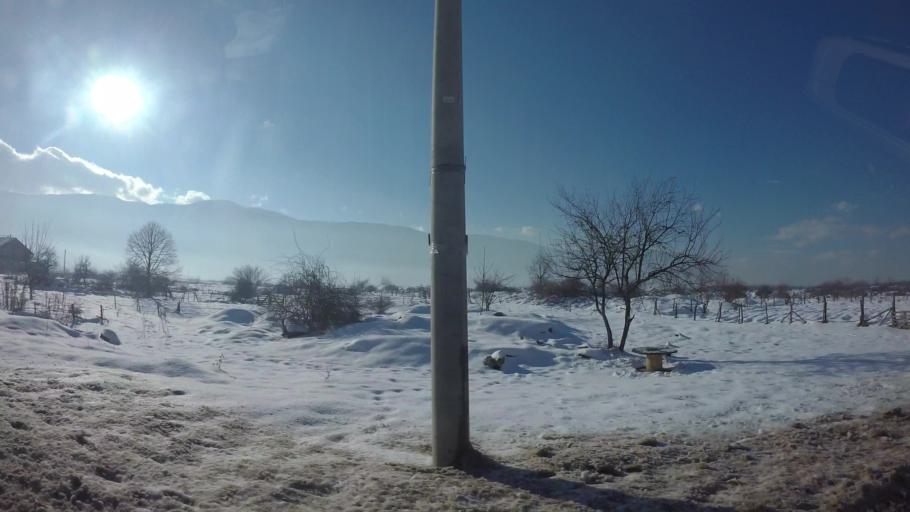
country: BA
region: Federation of Bosnia and Herzegovina
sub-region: Kanton Sarajevo
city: Sarajevo
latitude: 43.8100
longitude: 18.3278
